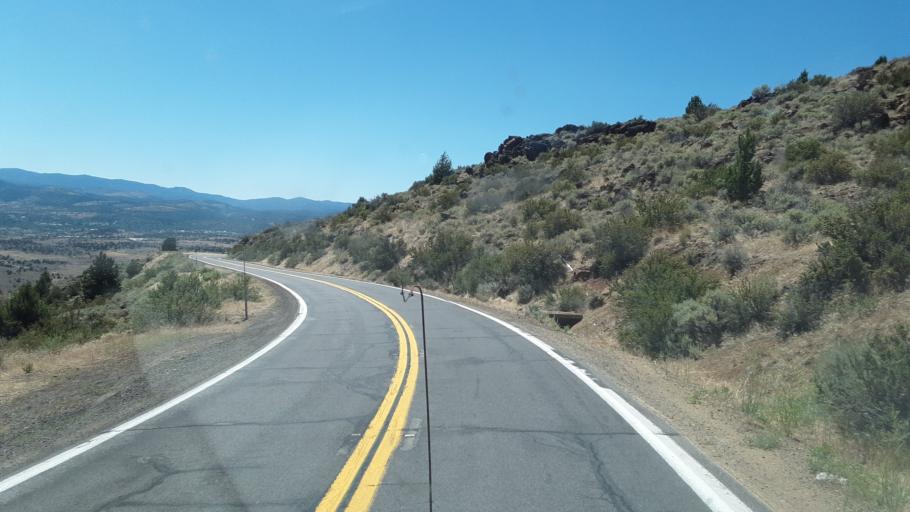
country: US
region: California
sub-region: Lassen County
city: Johnstonville
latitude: 40.4566
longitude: -120.5845
